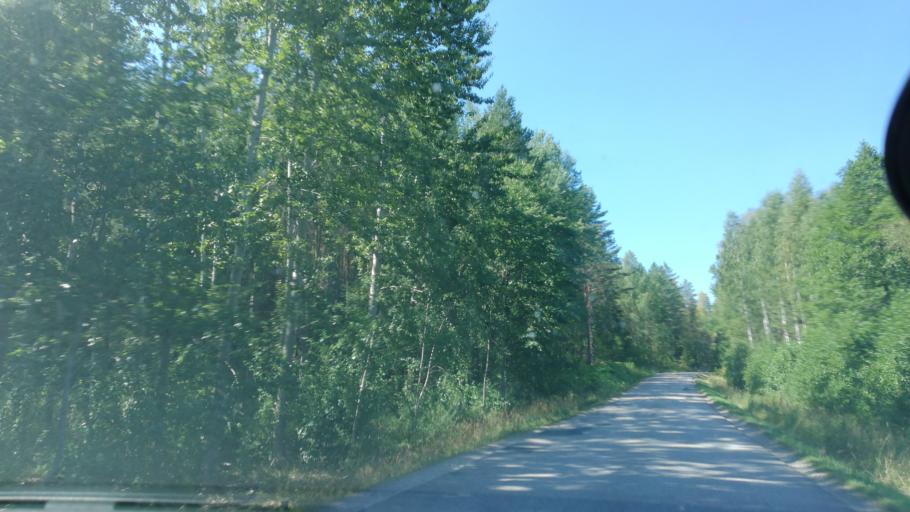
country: SE
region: OEstergoetland
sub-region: Finspangs Kommun
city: Finspang
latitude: 58.7288
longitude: 15.7451
